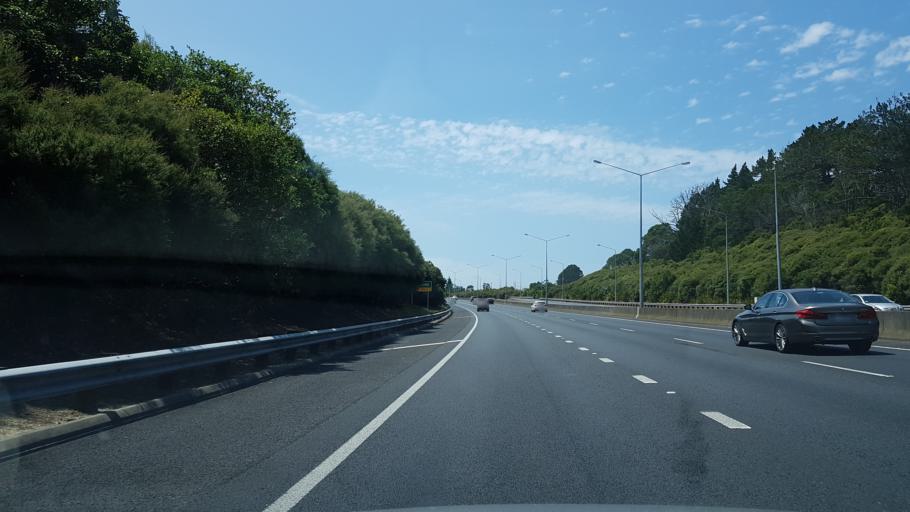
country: NZ
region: Auckland
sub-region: Auckland
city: Rothesay Bay
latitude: -36.7625
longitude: 174.6986
